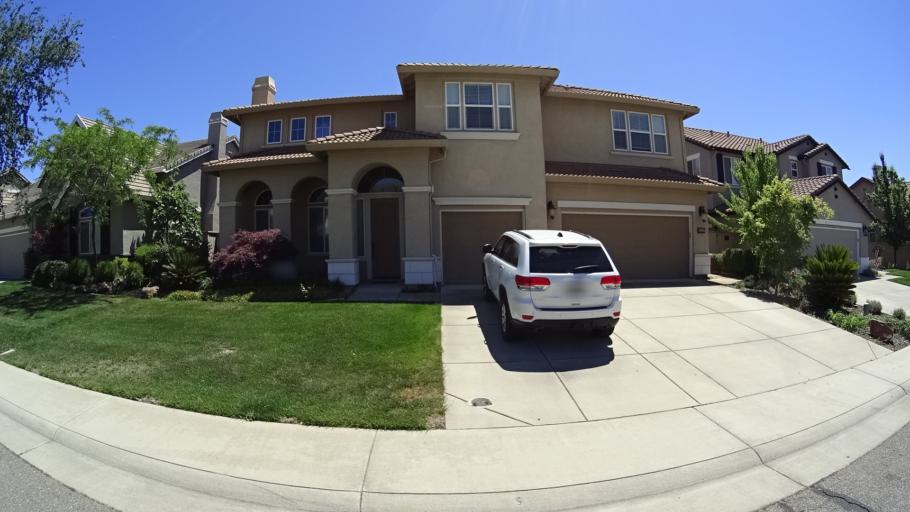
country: US
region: California
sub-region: Placer County
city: Rocklin
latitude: 38.8284
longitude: -121.2580
